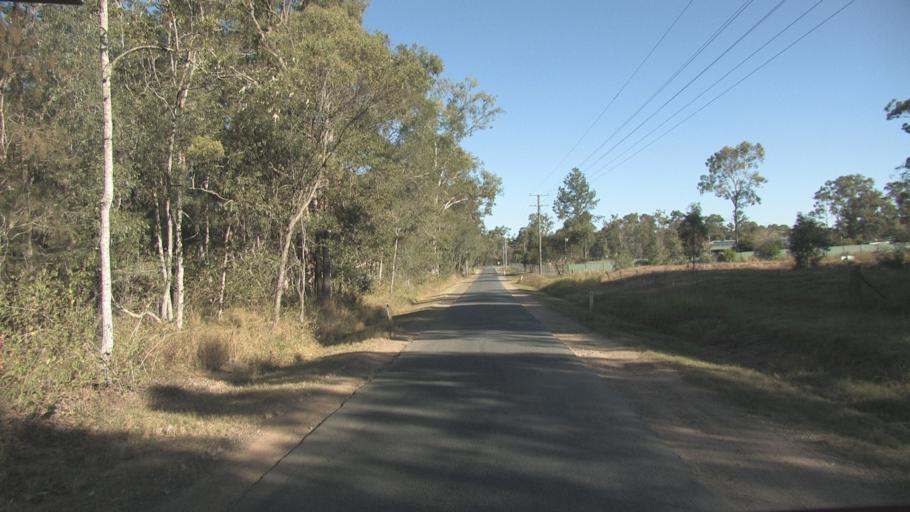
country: AU
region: Queensland
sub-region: Logan
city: North Maclean
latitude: -27.7888
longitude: 153.0384
